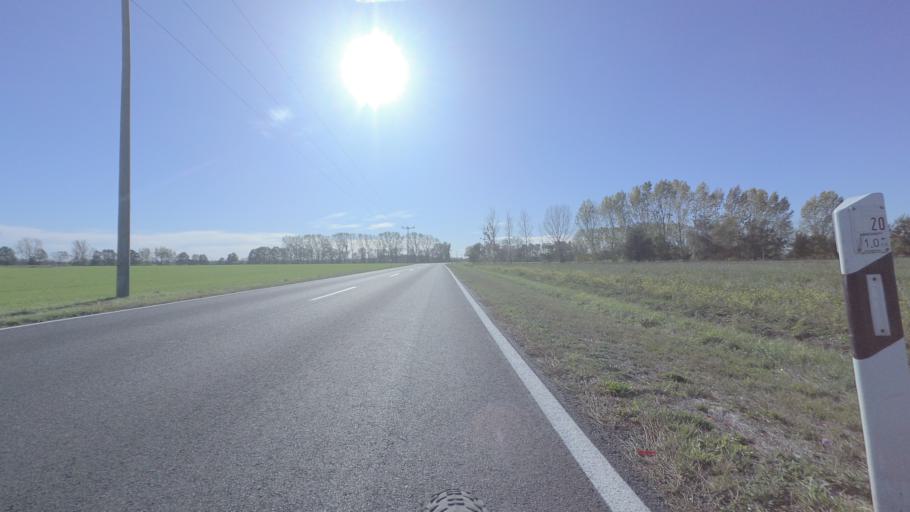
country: DE
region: Brandenburg
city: Elsterwerda
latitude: 51.4542
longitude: 13.4607
